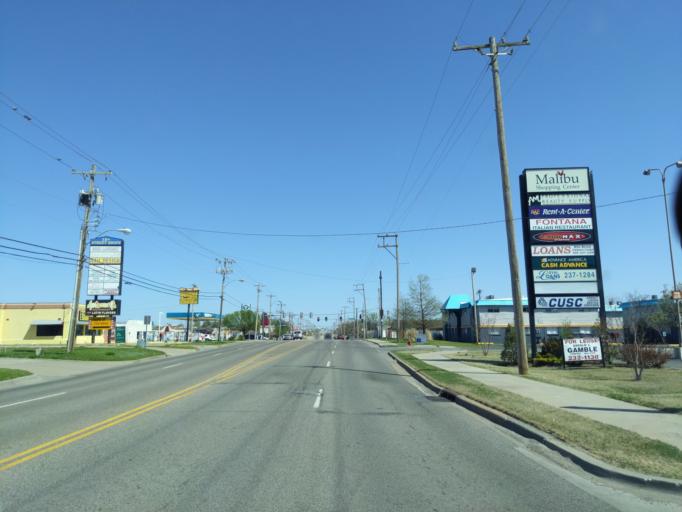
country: US
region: Oklahoma
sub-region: Cleveland County
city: Moore
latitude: 35.3488
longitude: -97.5045
